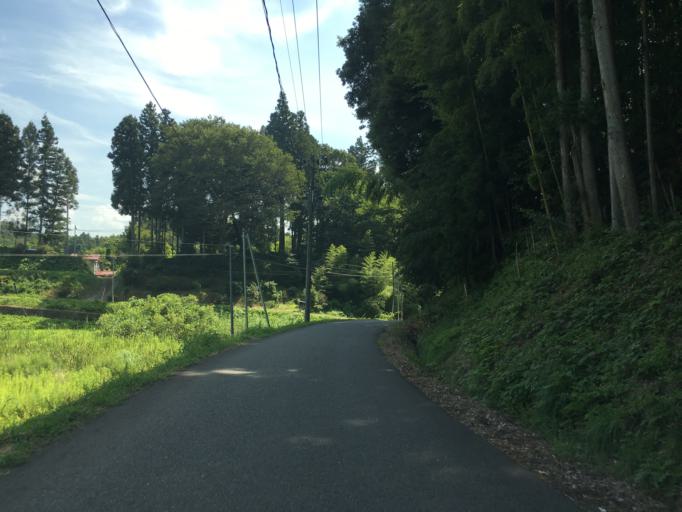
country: JP
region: Fukushima
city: Ishikawa
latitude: 37.1984
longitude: 140.4746
